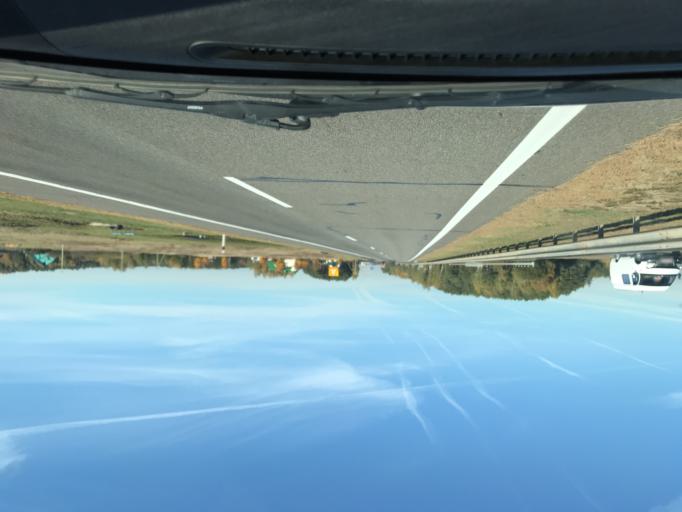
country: BY
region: Brest
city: Ivatsevichy
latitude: 52.7076
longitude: 25.3814
